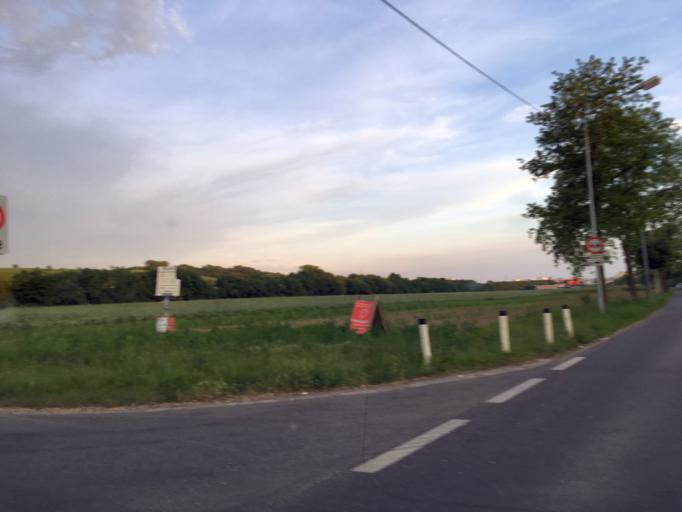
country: AT
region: Lower Austria
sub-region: Politischer Bezirk Wien-Umgebung
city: Gerasdorf bei Wien
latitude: 48.2742
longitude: 16.4575
